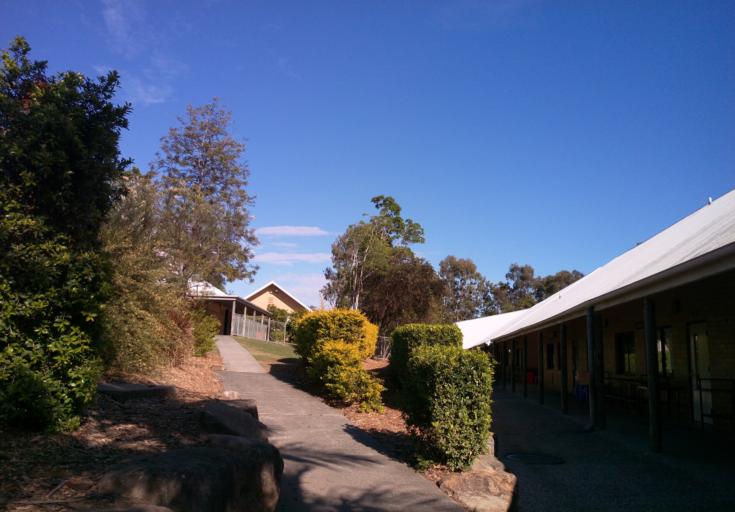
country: AU
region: Queensland
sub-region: Ipswich
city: Brassall
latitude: -27.5892
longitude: 152.7065
